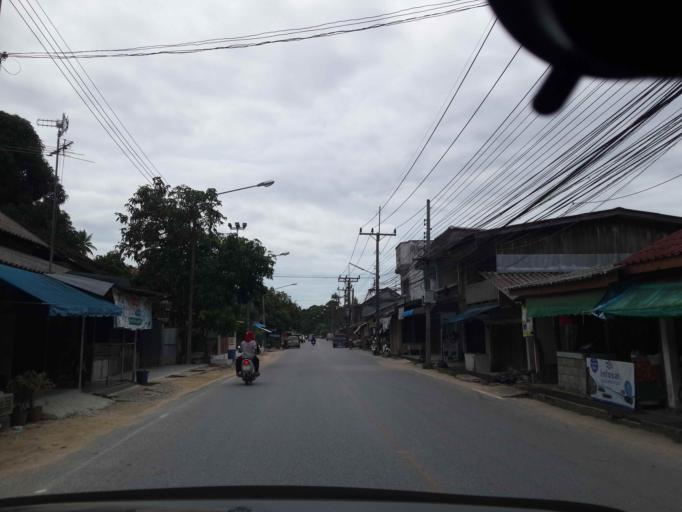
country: TH
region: Narathiwat
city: Yi-ngo
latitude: 6.3353
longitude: 101.6399
